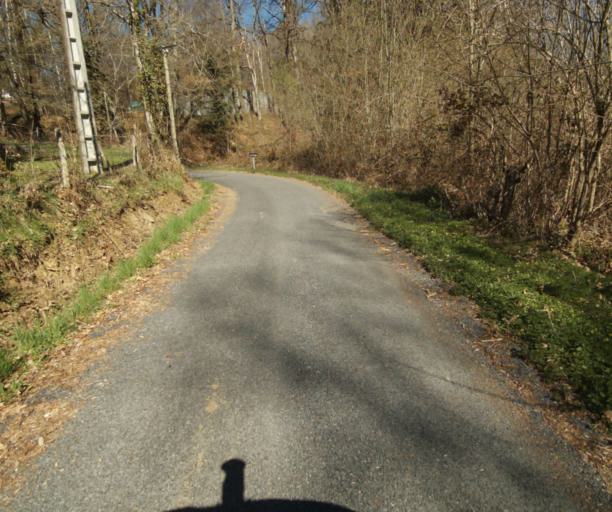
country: FR
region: Limousin
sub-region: Departement de la Correze
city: Saint-Clement
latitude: 45.3482
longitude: 1.6706
